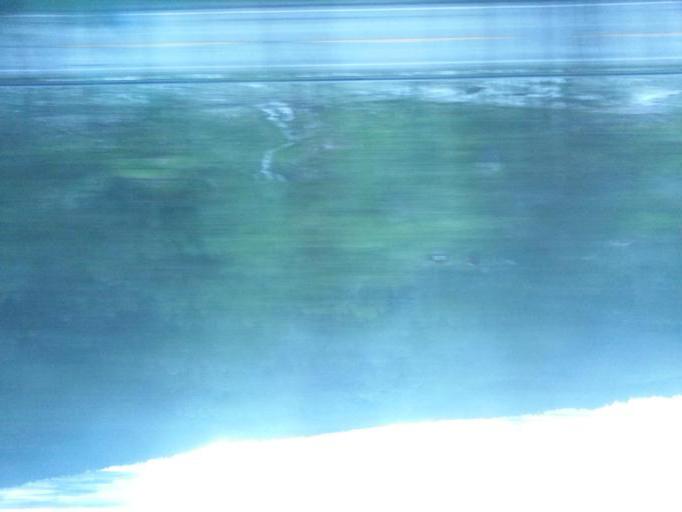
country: NO
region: Oppland
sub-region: Dovre
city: Dovre
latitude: 61.8970
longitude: 9.3908
